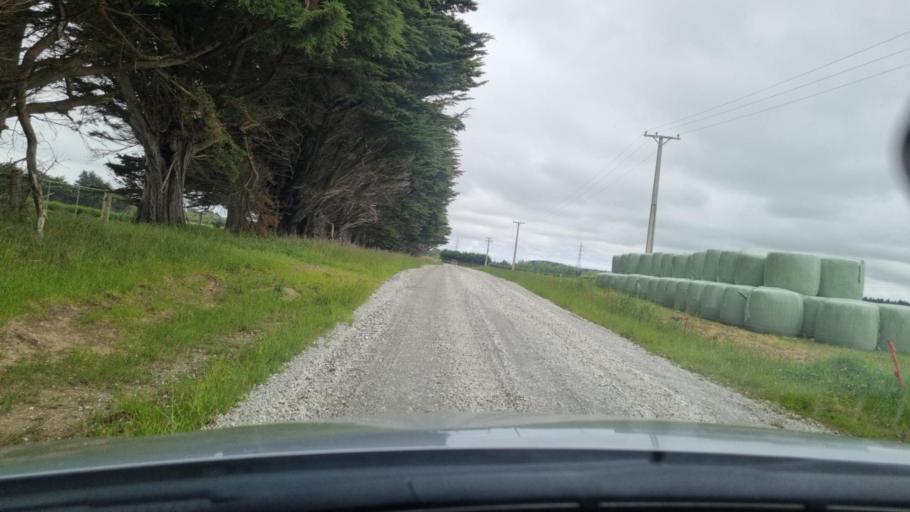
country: NZ
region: Southland
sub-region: Invercargill City
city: Invercargill
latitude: -46.4204
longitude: 168.4446
